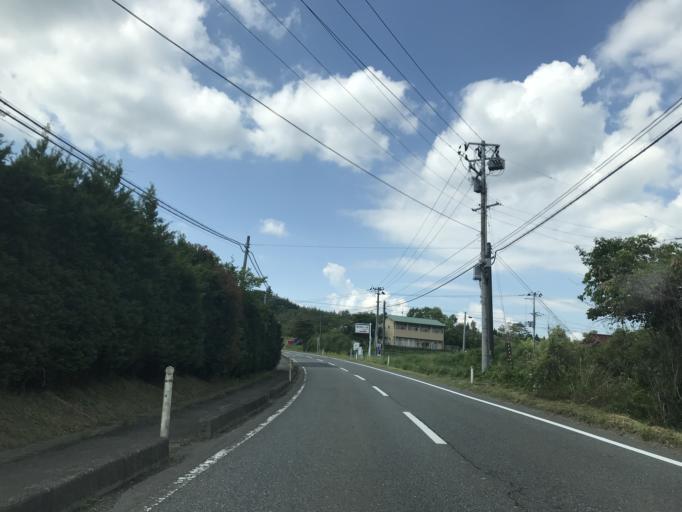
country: JP
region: Miyagi
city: Furukawa
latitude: 38.7651
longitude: 140.9600
